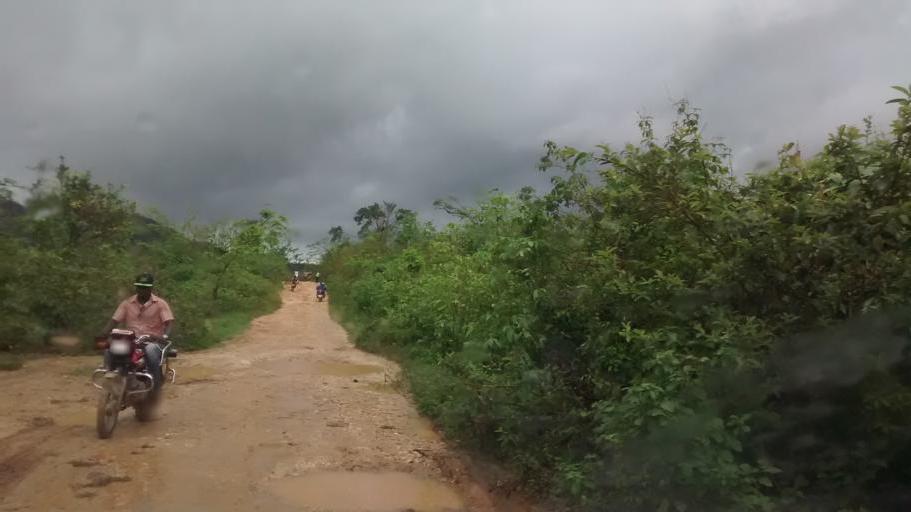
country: HT
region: Grandans
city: Corail
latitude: 18.5379
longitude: -73.9828
